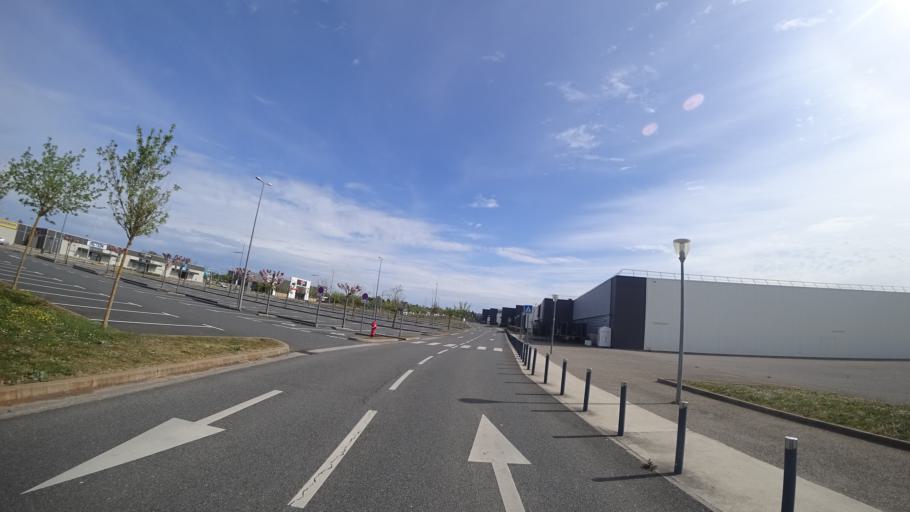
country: FR
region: Midi-Pyrenees
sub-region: Departement de l'Aveyron
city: Sebazac-Concoures
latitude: 44.3952
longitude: 2.6049
